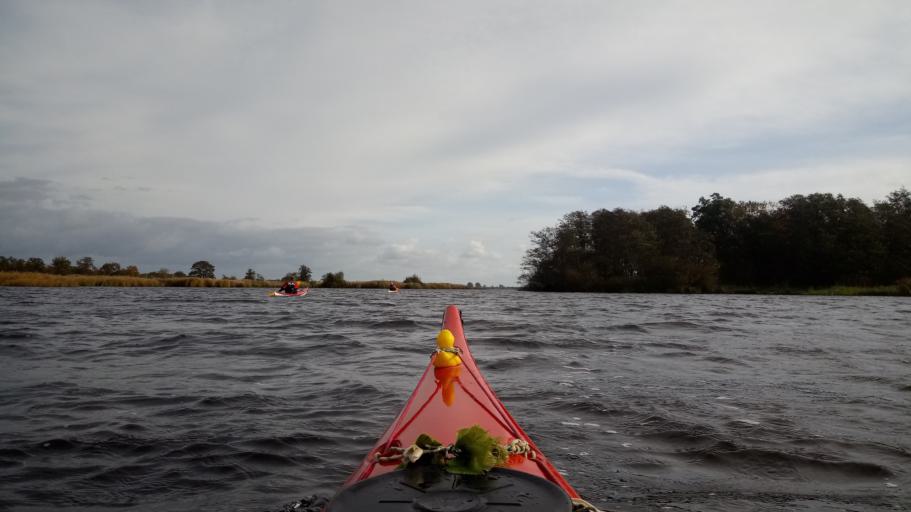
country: NL
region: Overijssel
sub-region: Gemeente Steenwijkerland
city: Sint Jansklooster
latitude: 52.6838
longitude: 6.0387
